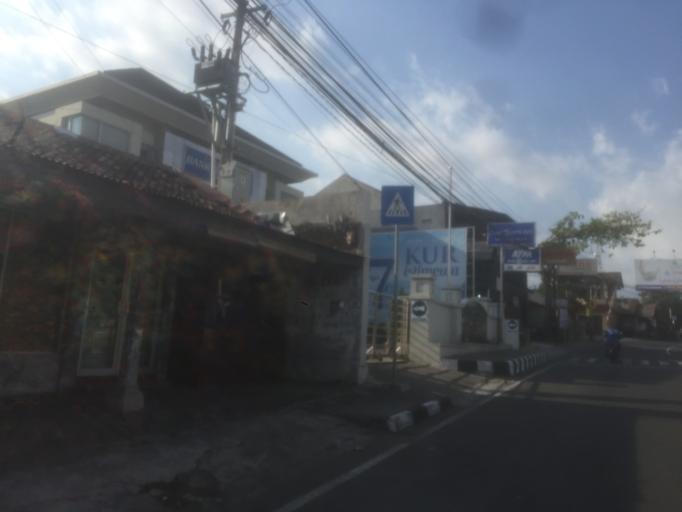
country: ID
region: Daerah Istimewa Yogyakarta
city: Sleman
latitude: -7.6618
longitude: 110.4207
